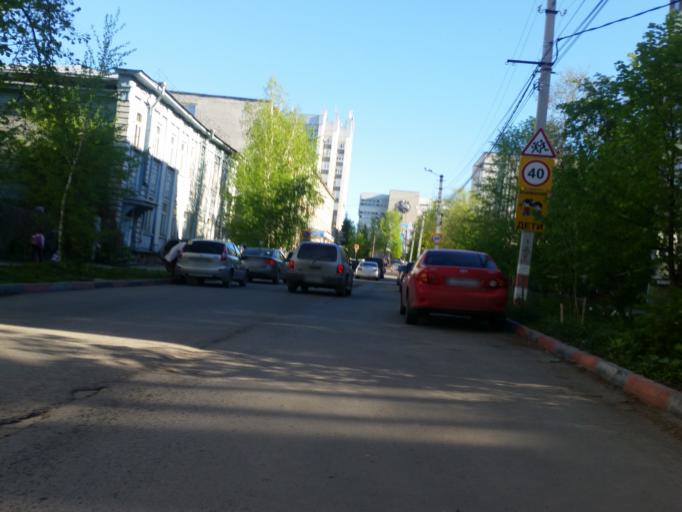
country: RU
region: Ulyanovsk
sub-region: Ulyanovskiy Rayon
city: Ulyanovsk
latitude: 54.3102
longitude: 48.3938
